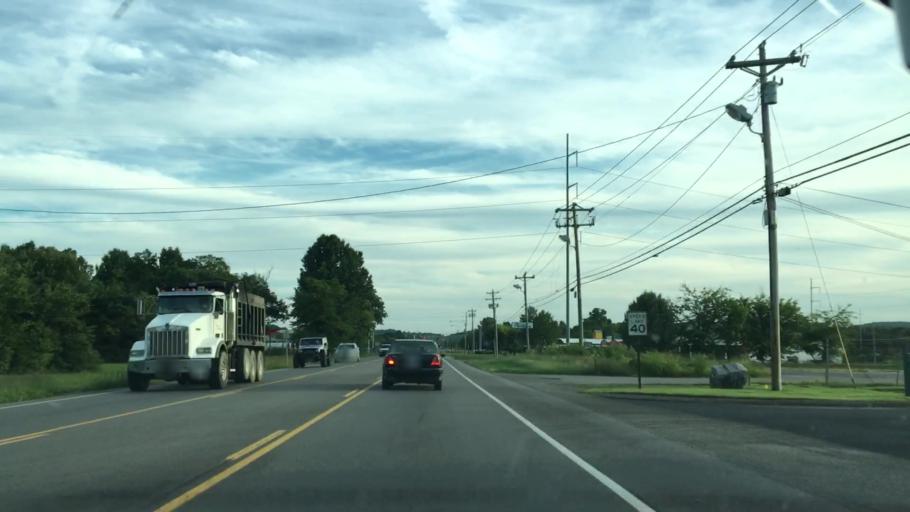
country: US
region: Tennessee
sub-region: Wilson County
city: Lebanon
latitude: 36.1767
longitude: -86.3015
